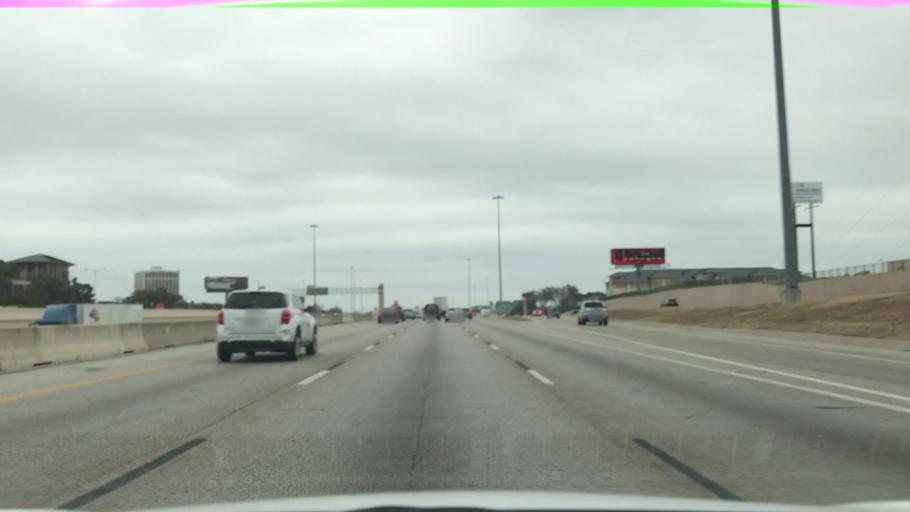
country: US
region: Texas
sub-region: Tarrant County
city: Arlington
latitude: 32.7597
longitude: -97.1138
